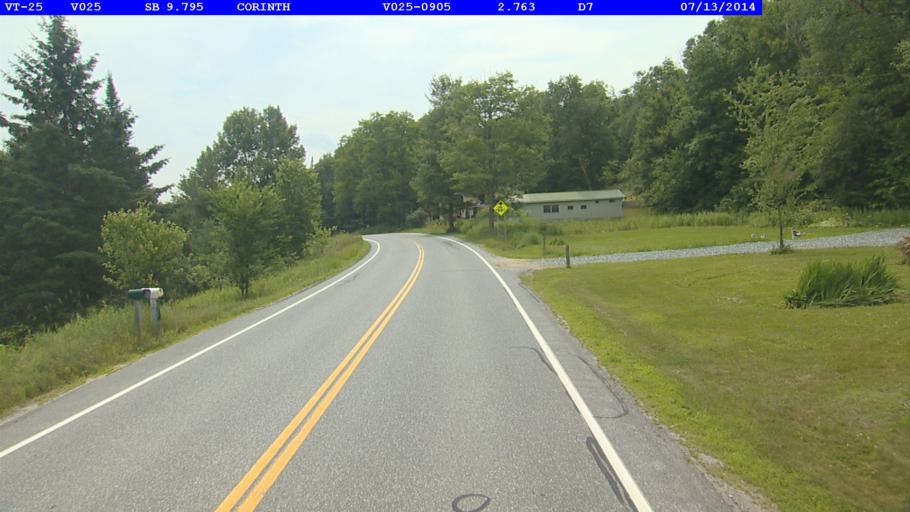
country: US
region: New Hampshire
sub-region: Grafton County
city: Haverhill
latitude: 44.0663
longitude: -72.2439
